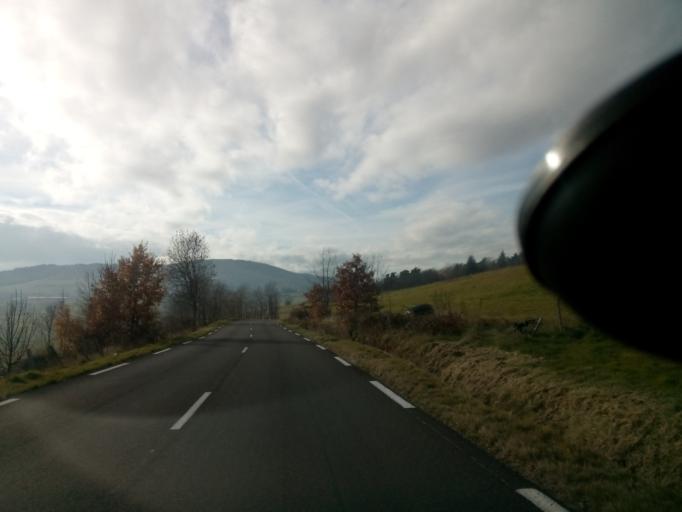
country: FR
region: Rhone-Alpes
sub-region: Departement de la Loire
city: Saint-Julien-Molin-Molette
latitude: 45.3288
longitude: 4.6363
